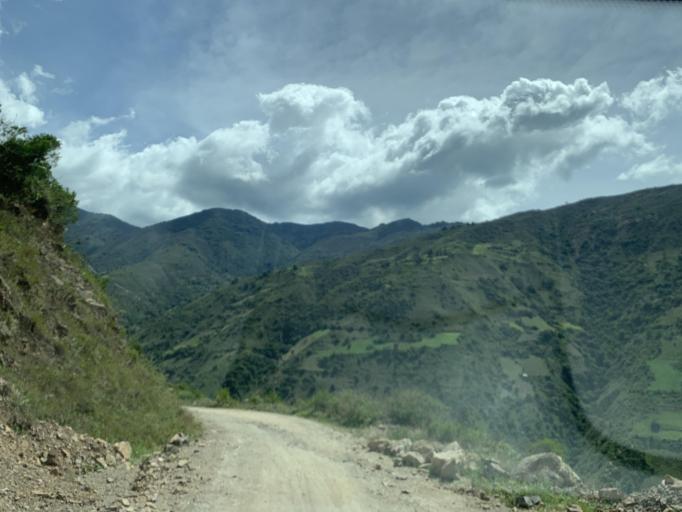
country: CO
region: Boyaca
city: Tipacoque
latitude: 6.4511
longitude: -72.7076
